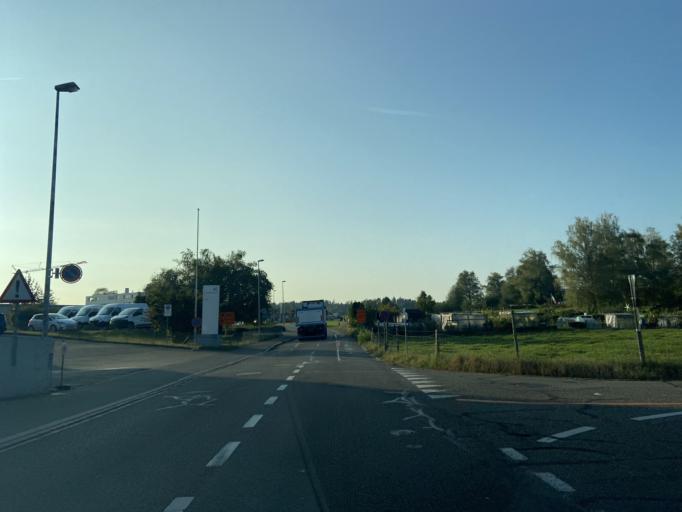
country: CH
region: Zurich
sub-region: Bezirk Pfaeffikon
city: Pfaeffikon / Pfaeffikon (Dorfkern)
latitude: 47.3660
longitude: 8.7731
